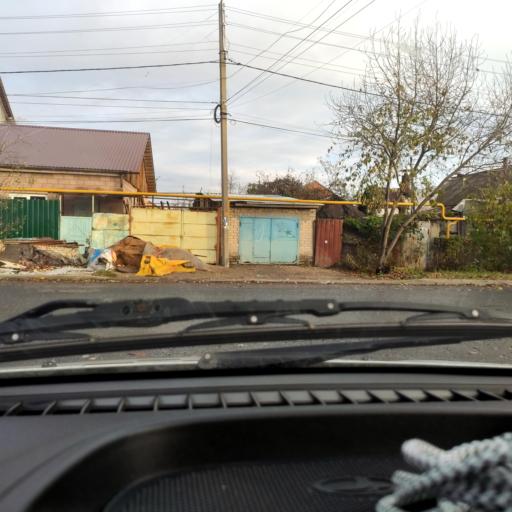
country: RU
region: Samara
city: Tol'yatti
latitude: 53.5274
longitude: 49.4101
